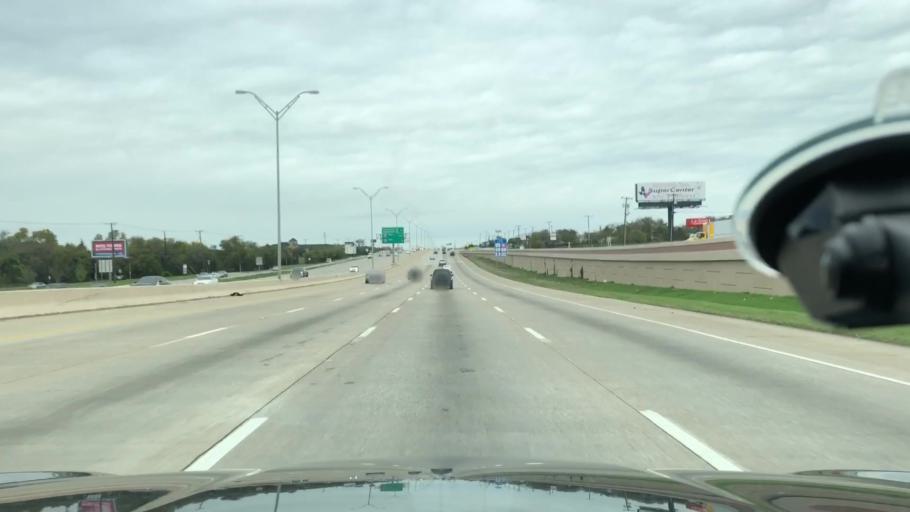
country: US
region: Texas
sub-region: Dallas County
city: DeSoto
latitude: 32.6109
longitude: -96.8229
